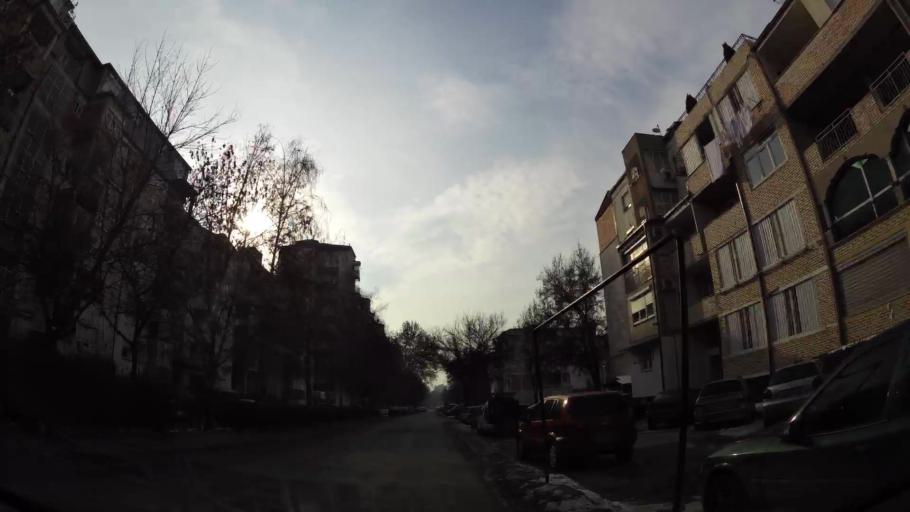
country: MK
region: Cair
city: Cair
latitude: 42.0219
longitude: 21.4320
